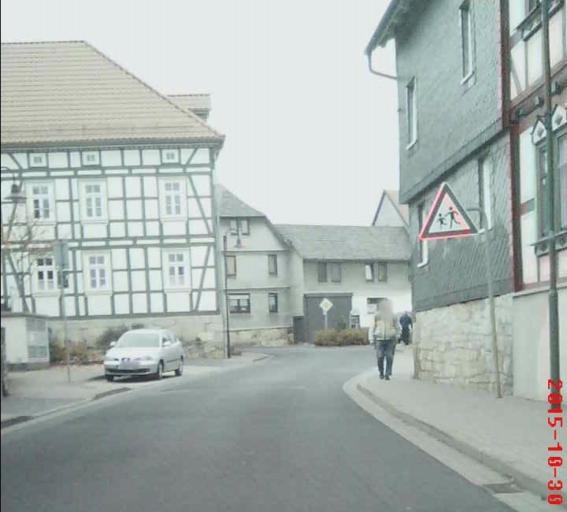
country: DE
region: Thuringia
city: Kullstedt
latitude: 51.2755
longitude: 10.2796
